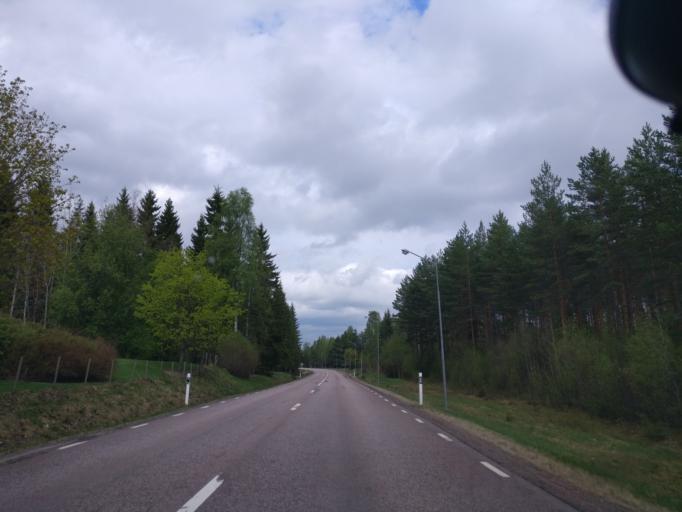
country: SE
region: Vaermland
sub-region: Hagfors Kommun
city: Ekshaerad
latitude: 60.1403
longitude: 13.5252
